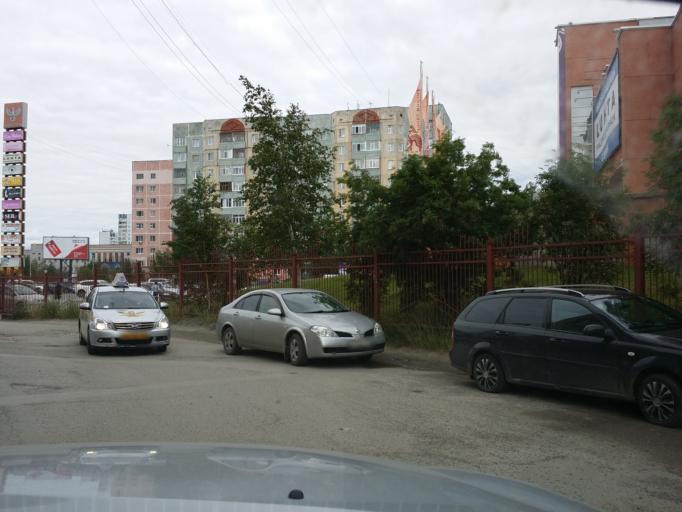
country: RU
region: Khanty-Mansiyskiy Avtonomnyy Okrug
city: Nizhnevartovsk
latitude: 60.9312
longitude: 76.5908
